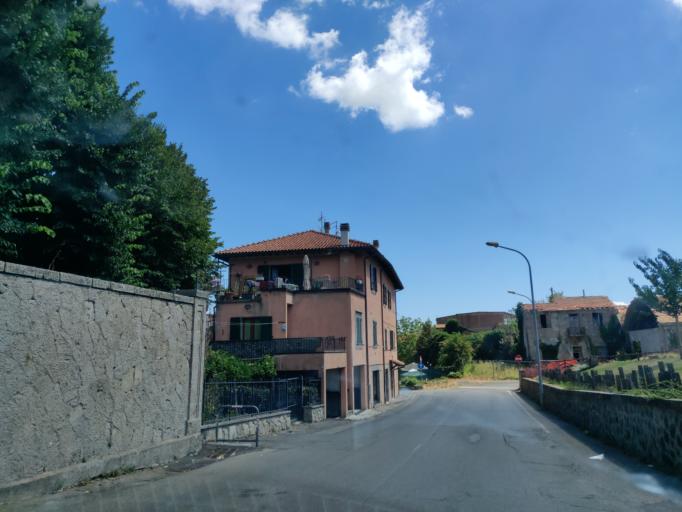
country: IT
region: Tuscany
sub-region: Provincia di Siena
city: Abbadia San Salvatore
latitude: 42.8791
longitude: 11.6738
